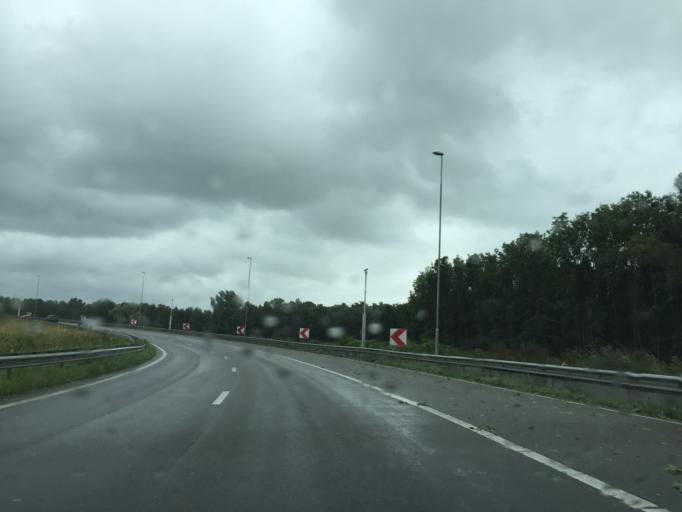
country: NL
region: North Holland
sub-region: Gemeente Weesp
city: Weesp
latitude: 52.3151
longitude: 5.0997
